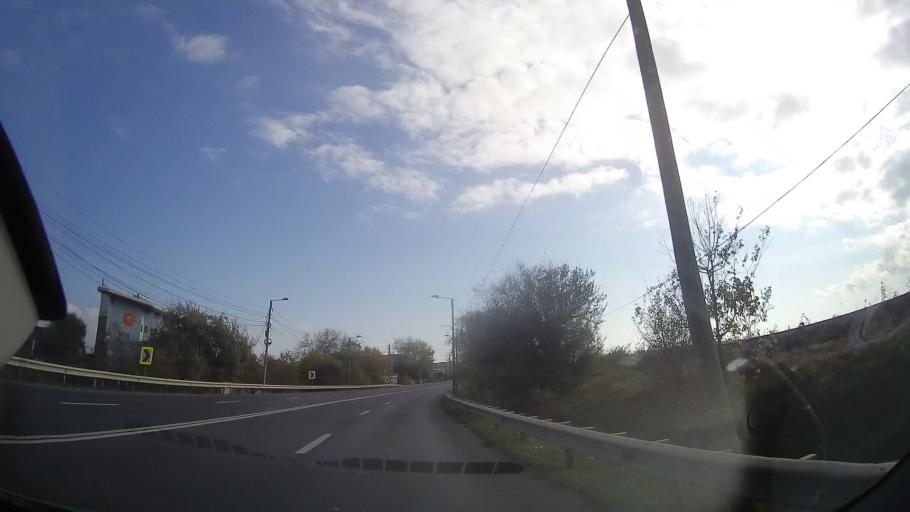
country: RO
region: Constanta
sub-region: Oras Eforie
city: Eforie Nord
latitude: 44.0577
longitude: 28.6377
